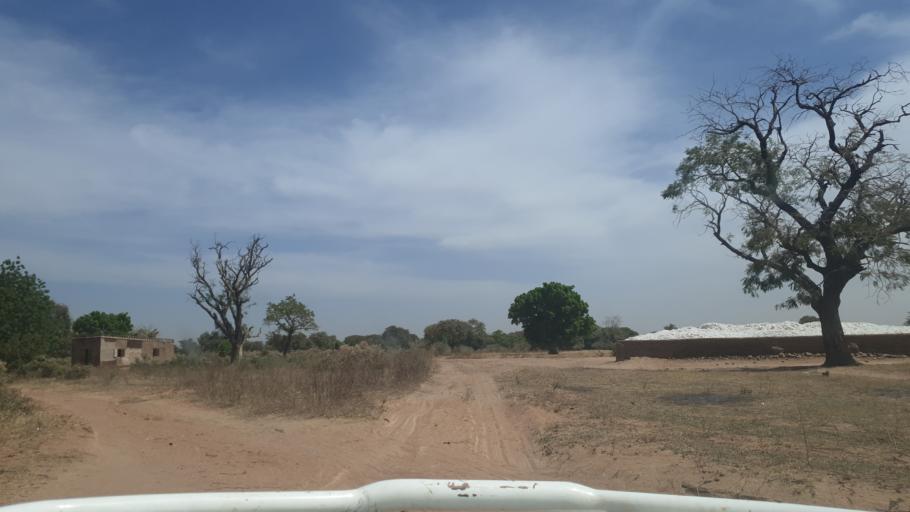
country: ML
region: Sikasso
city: Yorosso
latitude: 12.2833
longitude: -4.6836
